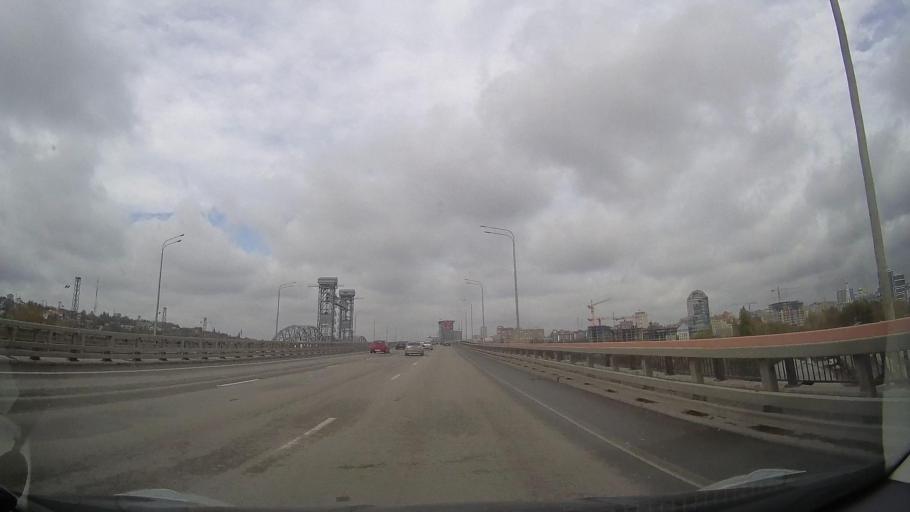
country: RU
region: Rostov
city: Rostov-na-Donu
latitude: 47.2072
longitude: 39.7051
